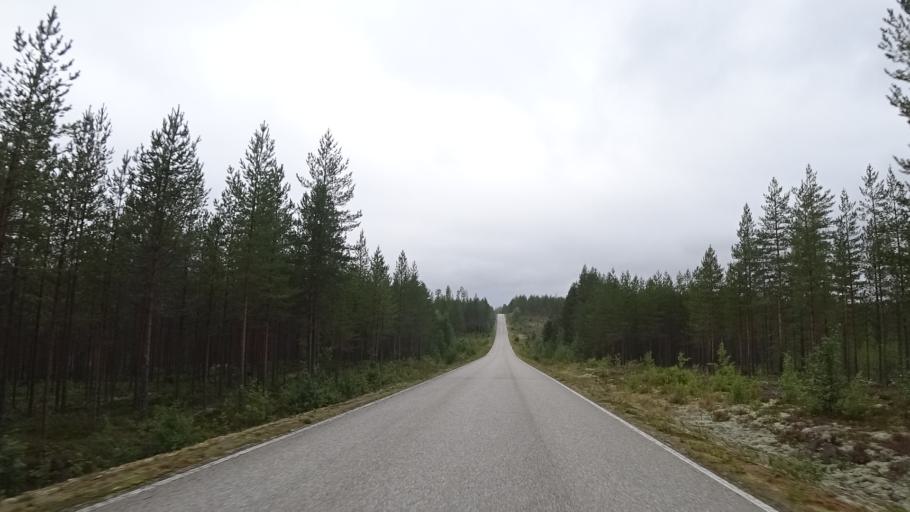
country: FI
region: North Karelia
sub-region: Pielisen Karjala
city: Lieksa
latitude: 63.3816
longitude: 30.3216
